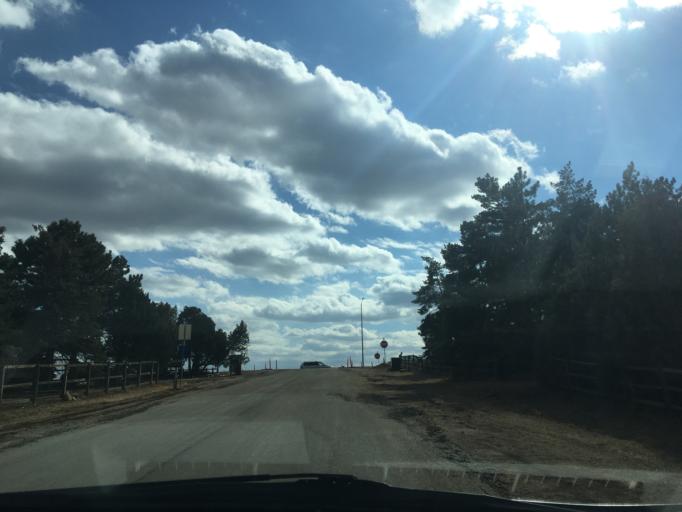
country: US
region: Colorado
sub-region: Boulder County
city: Lafayette
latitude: 39.9585
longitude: -105.0600
